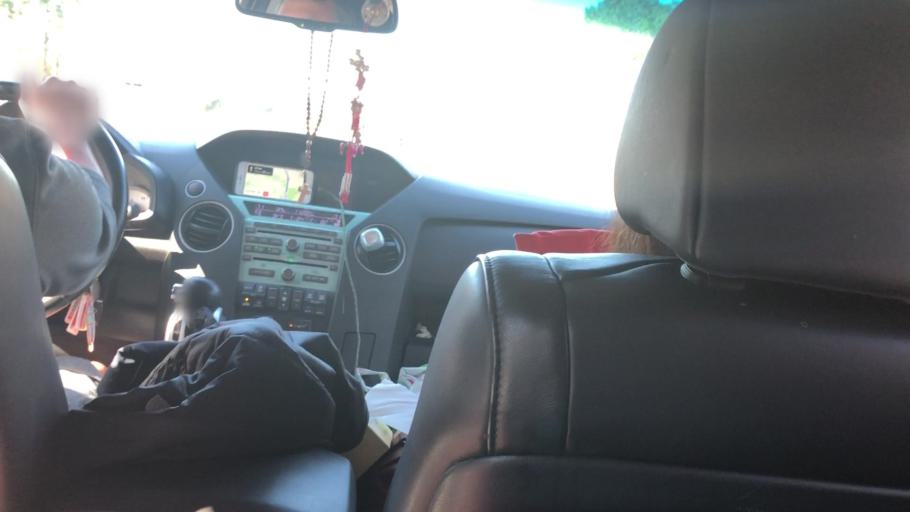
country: US
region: Louisiana
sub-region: Saint John the Baptist Parish
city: Montegut
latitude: 30.1020
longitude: -90.4863
